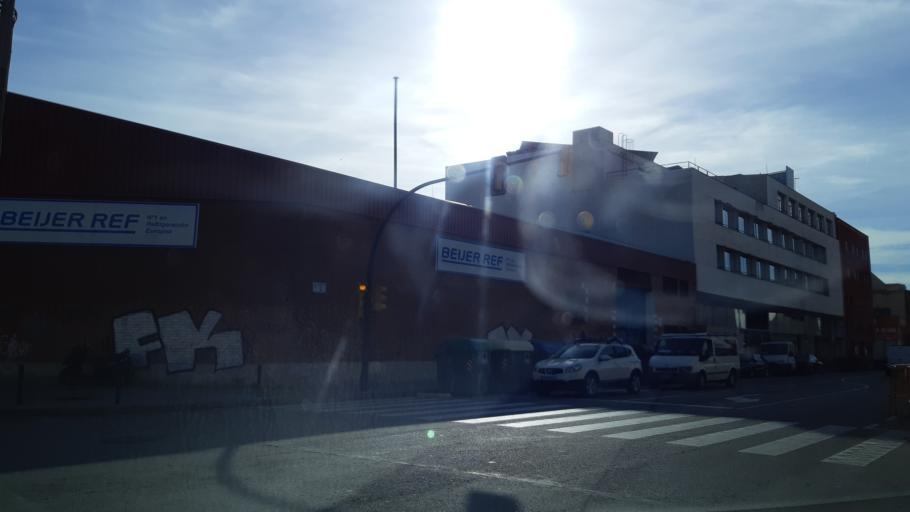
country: ES
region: Catalonia
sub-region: Provincia de Barcelona
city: L'Hospitalet de Llobregat
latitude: 41.3569
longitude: 2.1094
